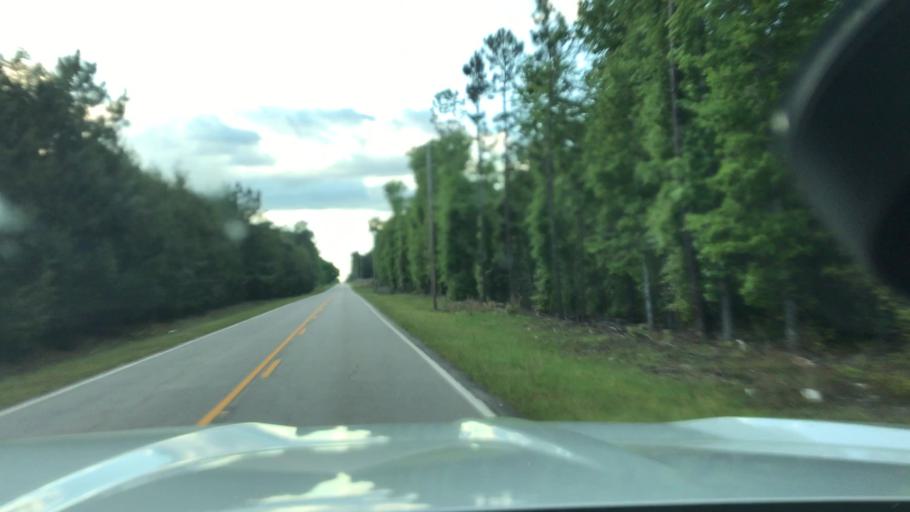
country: US
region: South Carolina
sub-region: Bamberg County
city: Denmark
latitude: 33.4557
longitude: -81.1418
